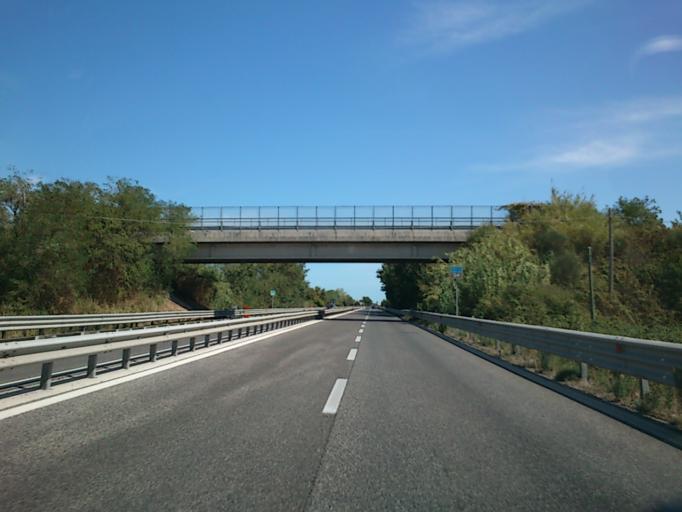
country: IT
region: The Marches
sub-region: Provincia di Pesaro e Urbino
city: Cuccurano
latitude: 43.7773
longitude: 12.9798
